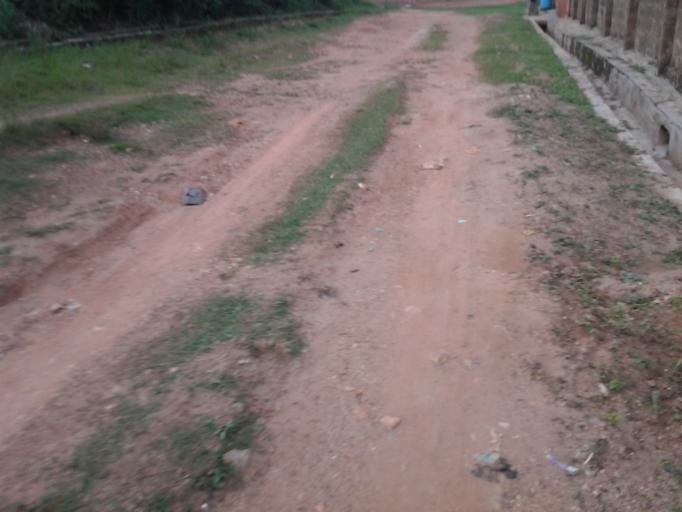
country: NG
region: Oyo
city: Ibadan
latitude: 7.4349
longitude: 3.9471
